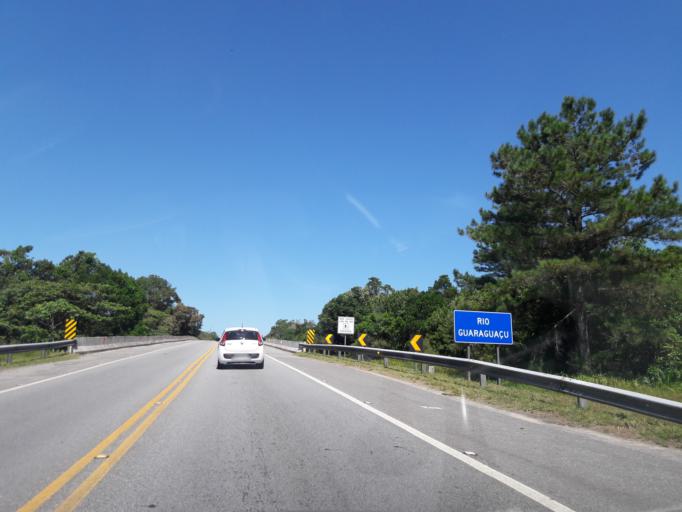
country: BR
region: Parana
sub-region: Pontal Do Parana
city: Pontal do Parana
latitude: -25.6711
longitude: -48.5143
